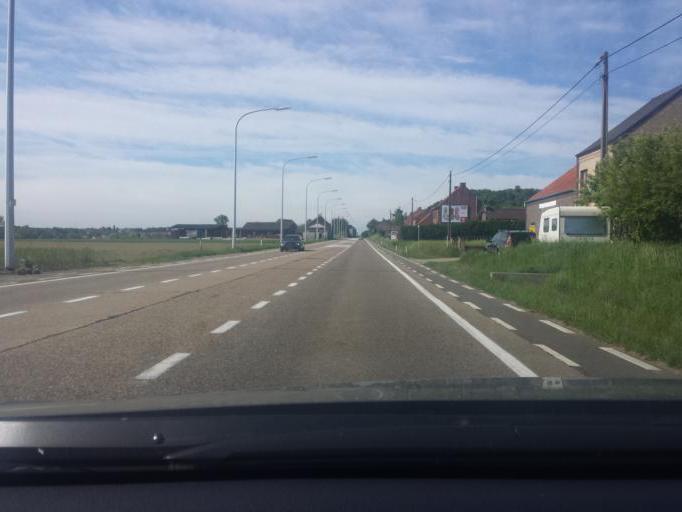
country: BE
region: Flanders
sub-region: Provincie Vlaams-Brabant
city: Diest
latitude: 50.9647
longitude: 5.0282
